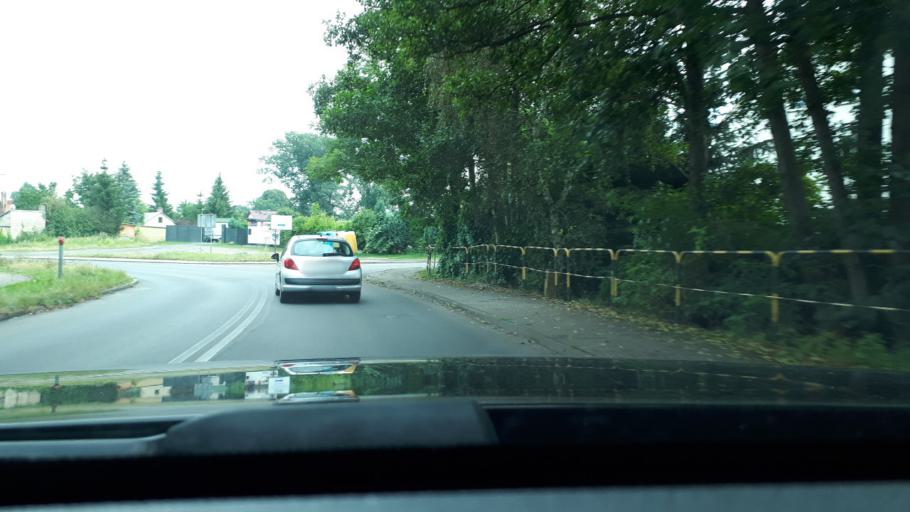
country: PL
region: Lower Silesian Voivodeship
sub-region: Powiat lubanski
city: Luban
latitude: 51.1085
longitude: 15.2895
